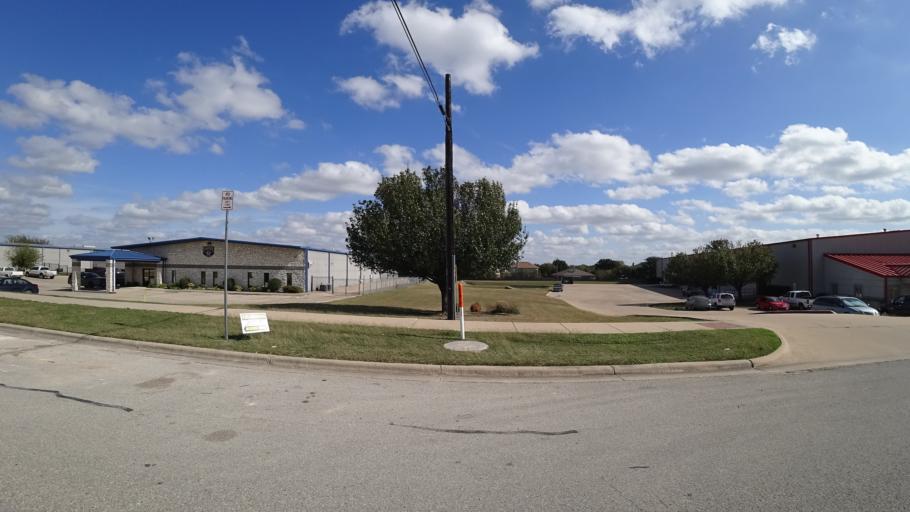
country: US
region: Texas
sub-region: Travis County
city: Windemere
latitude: 30.4598
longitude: -97.6600
